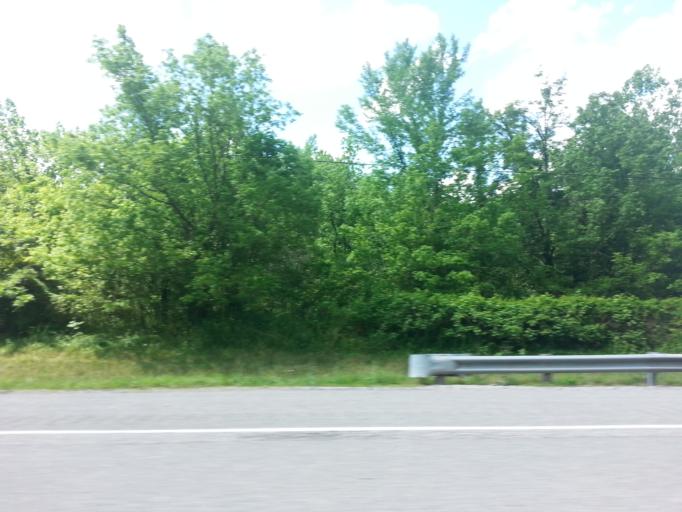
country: US
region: Kentucky
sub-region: Harlan County
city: Harlan
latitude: 36.8721
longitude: -83.3054
